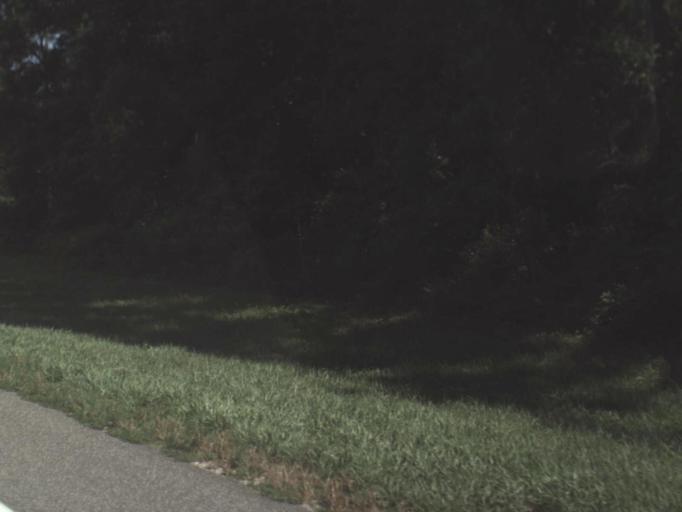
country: US
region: Florida
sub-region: Lafayette County
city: Mayo
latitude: 30.0457
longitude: -83.0797
